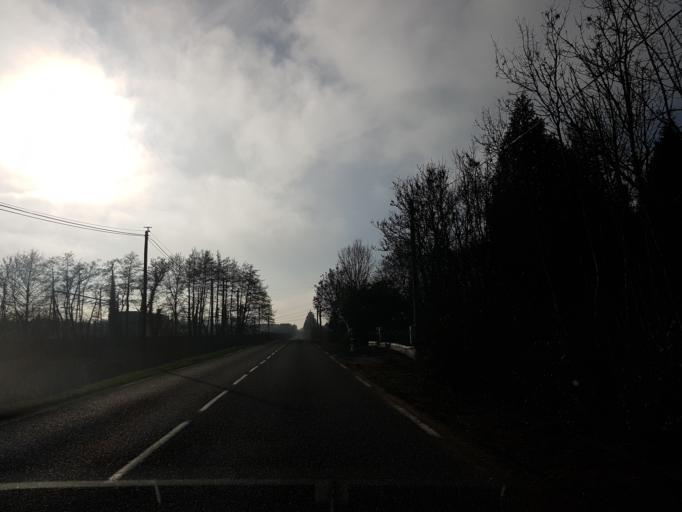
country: FR
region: Bourgogne
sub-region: Departement de Saone-et-Loire
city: Gueugnon
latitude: 46.6118
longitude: 4.0763
